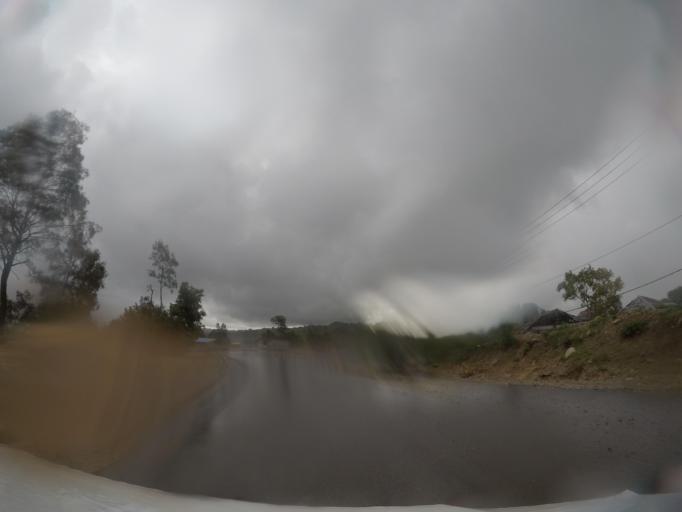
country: TL
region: Baucau
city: Venilale
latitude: -8.6367
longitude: 126.3772
